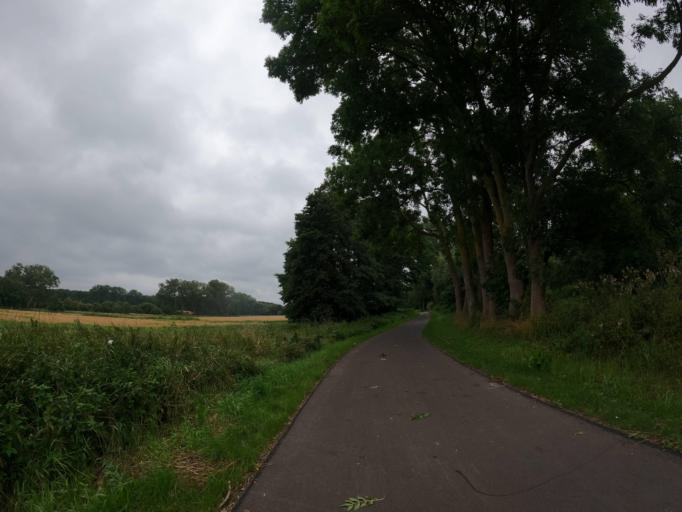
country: DE
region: Mecklenburg-Vorpommern
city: Poseritz
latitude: 54.2834
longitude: 13.2335
